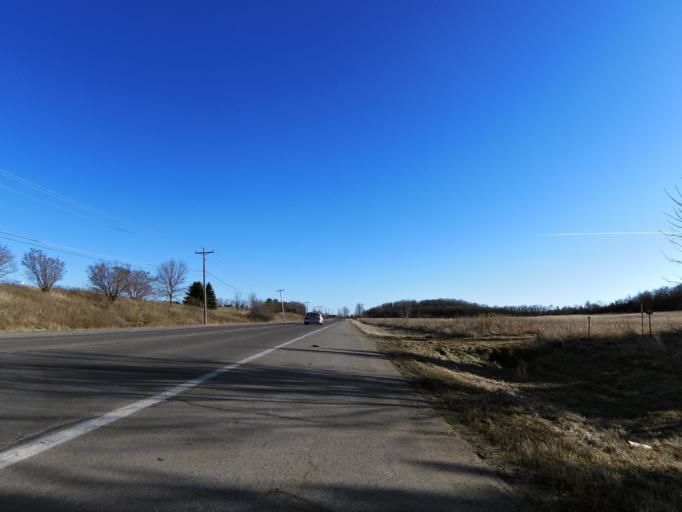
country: US
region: Minnesota
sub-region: Washington County
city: Bayport
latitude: 44.9927
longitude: -92.7909
